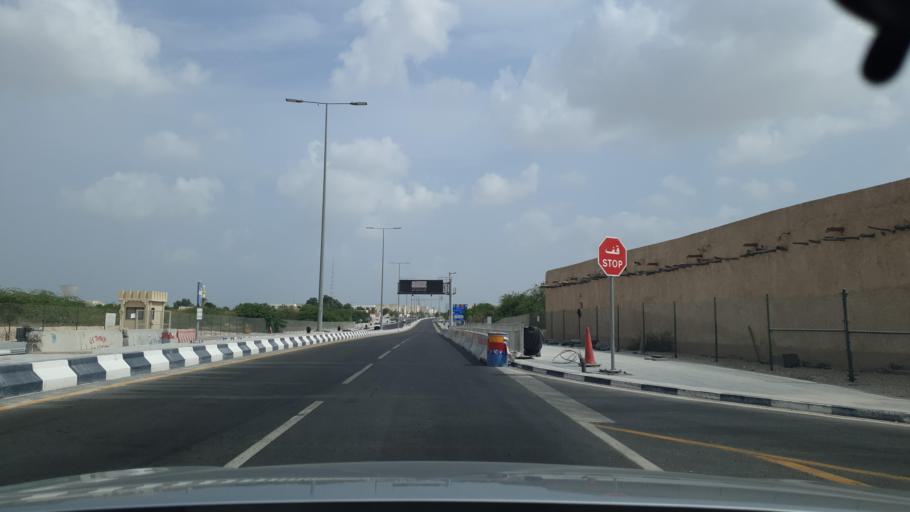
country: QA
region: Baladiyat ar Rayyan
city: Ar Rayyan
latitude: 25.2765
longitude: 51.4512
